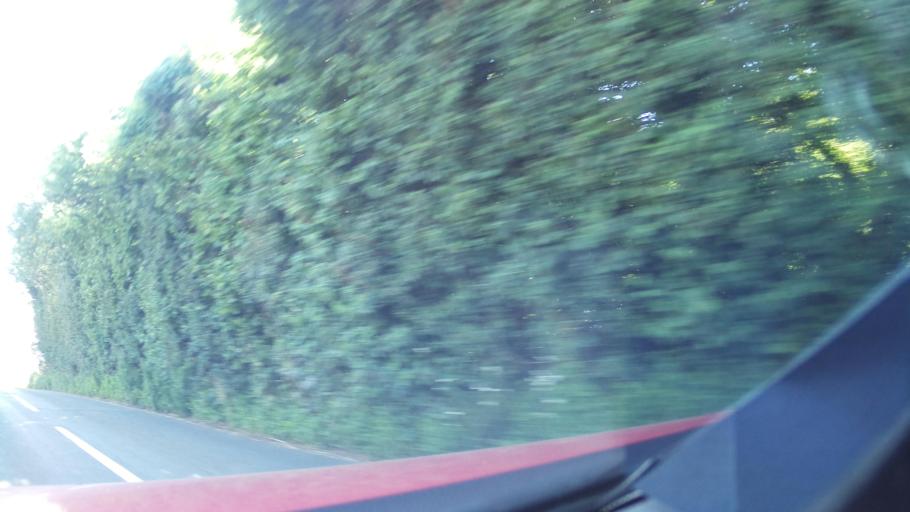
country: GB
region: England
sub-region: West Berkshire
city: Winterbourne
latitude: 51.4700
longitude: -1.3538
